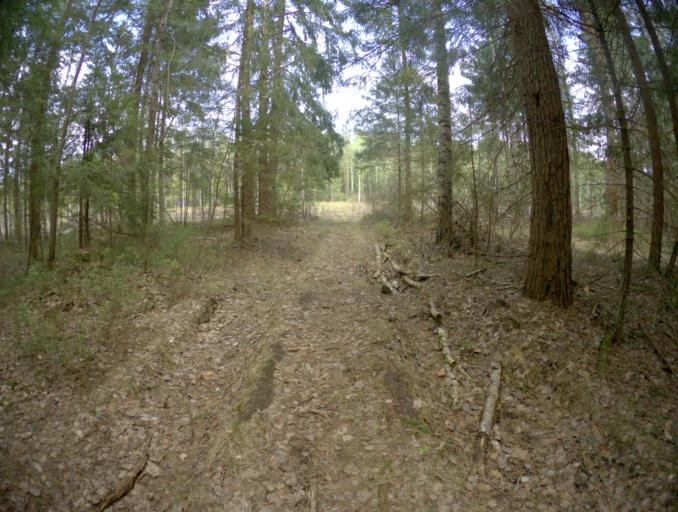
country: RU
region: Vladimir
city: Golovino
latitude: 55.9066
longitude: 40.4952
